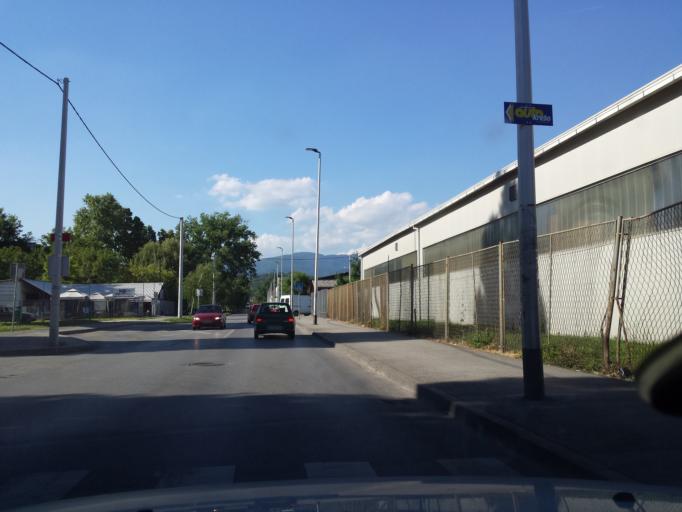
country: HR
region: Grad Zagreb
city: Jankomir
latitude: 45.8053
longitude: 15.9301
